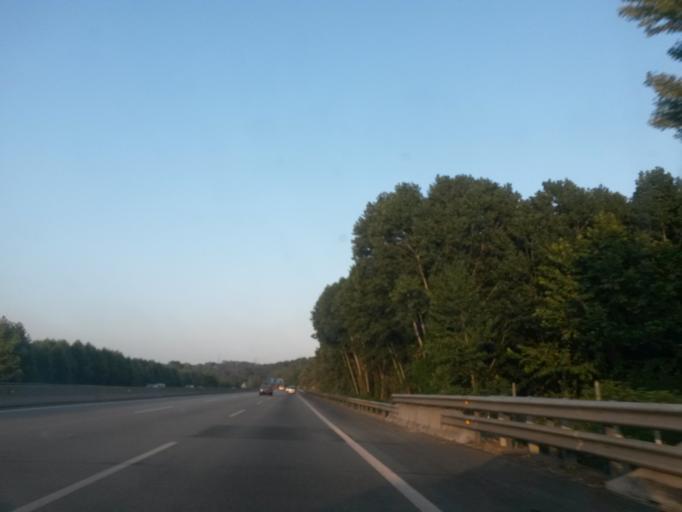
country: ES
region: Catalonia
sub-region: Provincia de Girona
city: Hostalric
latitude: 41.7292
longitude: 2.6214
